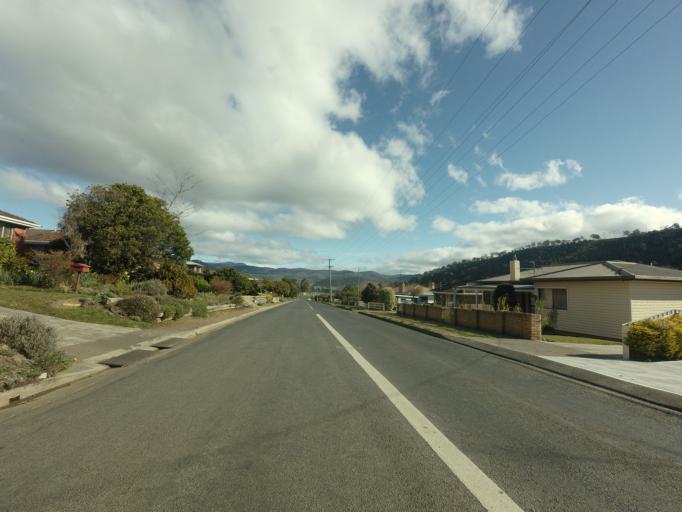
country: AU
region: Tasmania
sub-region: Derwent Valley
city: New Norfolk
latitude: -42.7560
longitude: 147.0516
